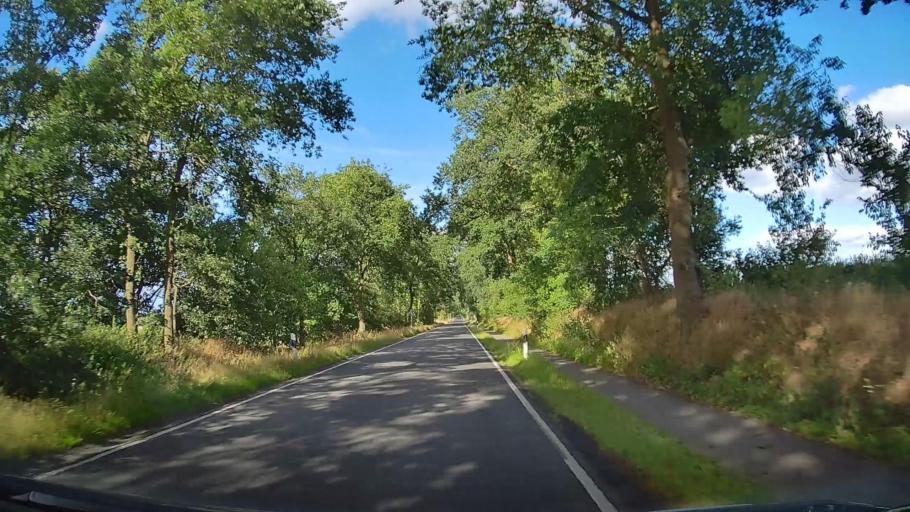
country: DE
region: Lower Saxony
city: Vrees
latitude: 52.9125
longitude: 7.8499
